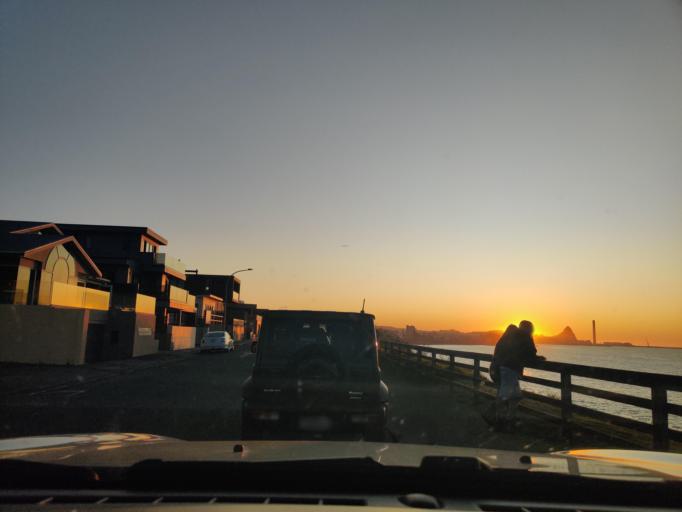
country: NZ
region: Taranaki
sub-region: New Plymouth District
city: New Plymouth
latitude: -39.0519
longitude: 174.0807
